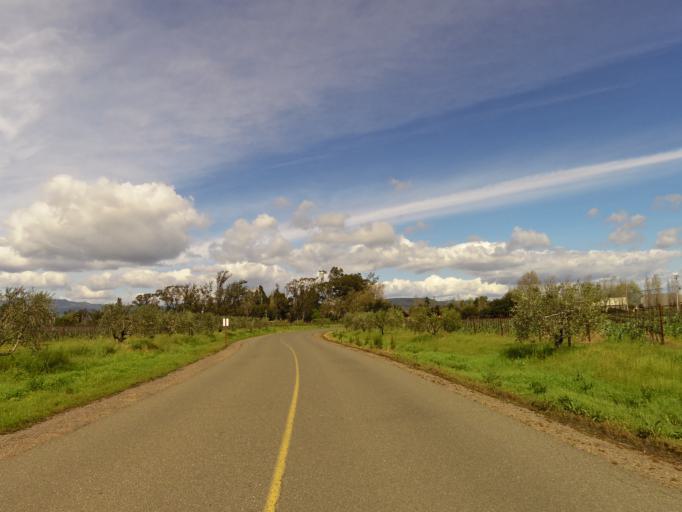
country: US
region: California
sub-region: Sonoma County
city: Temelec
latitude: 38.2268
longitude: -122.4603
